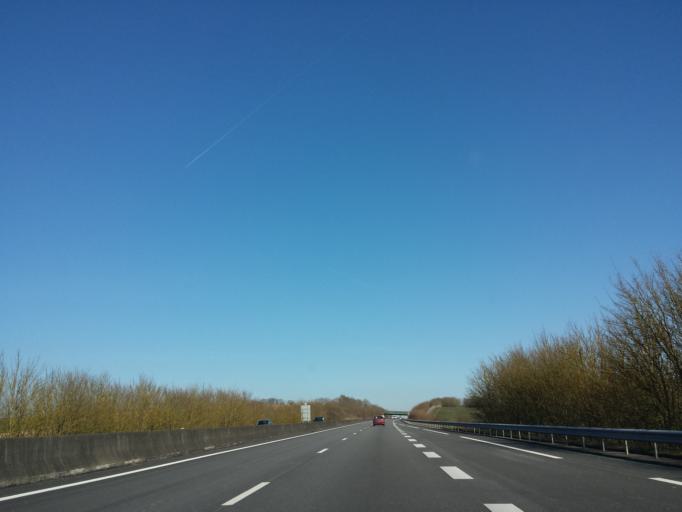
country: FR
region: Picardie
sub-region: Departement de l'Oise
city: Saint-Sulpice
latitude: 49.3684
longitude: 2.1084
